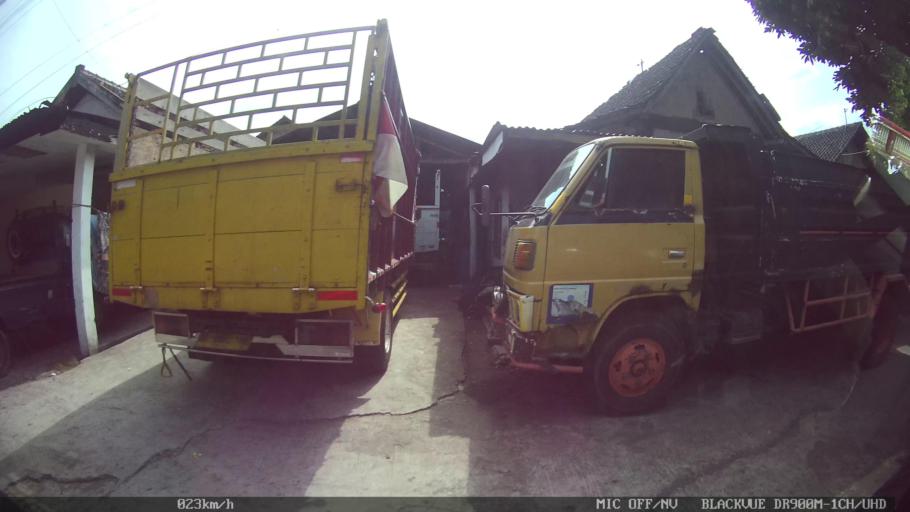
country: ID
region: Daerah Istimewa Yogyakarta
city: Depok
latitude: -7.7753
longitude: 110.4356
